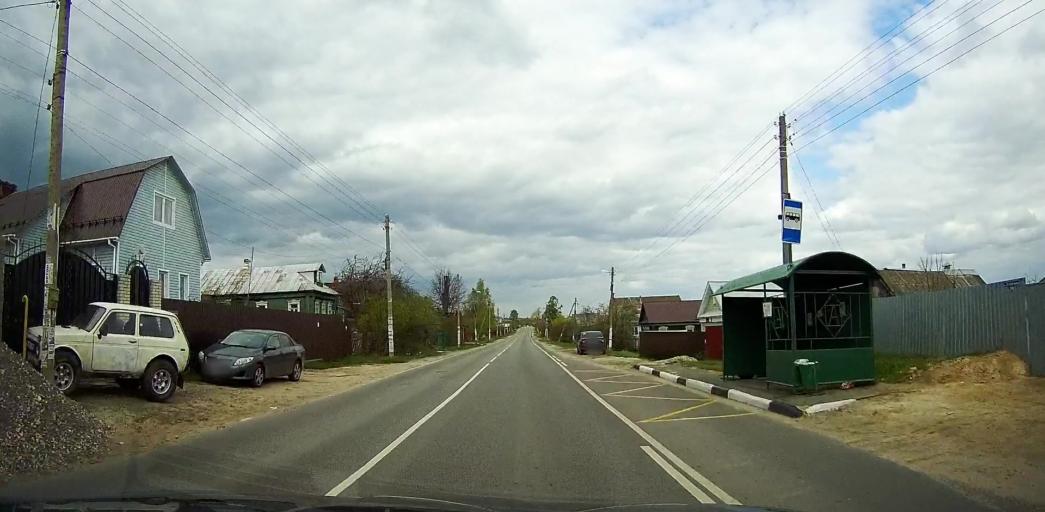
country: RU
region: Moskovskaya
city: Ashitkovo
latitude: 55.4541
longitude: 38.5949
